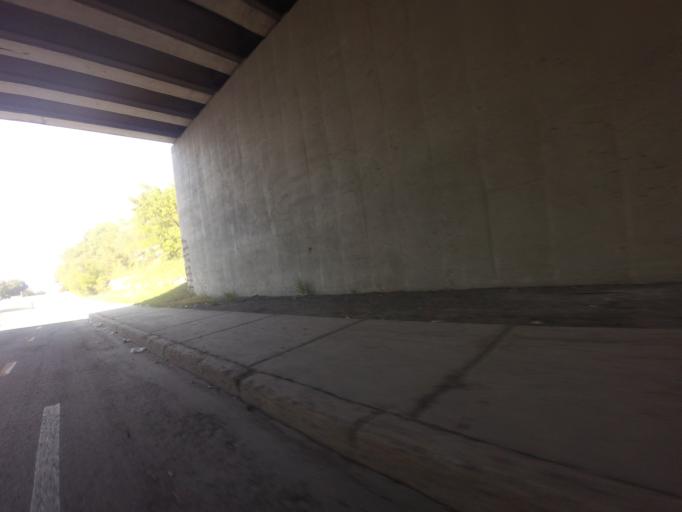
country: CA
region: Quebec
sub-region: Laurentides
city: Saint-Eustache
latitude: 45.5638
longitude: -73.9184
